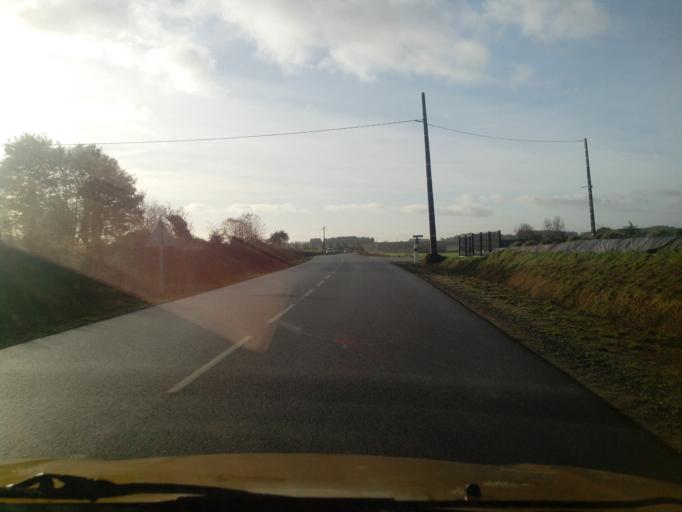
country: FR
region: Brittany
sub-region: Departement du Morbihan
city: Meneac
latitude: 48.1261
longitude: -2.4594
